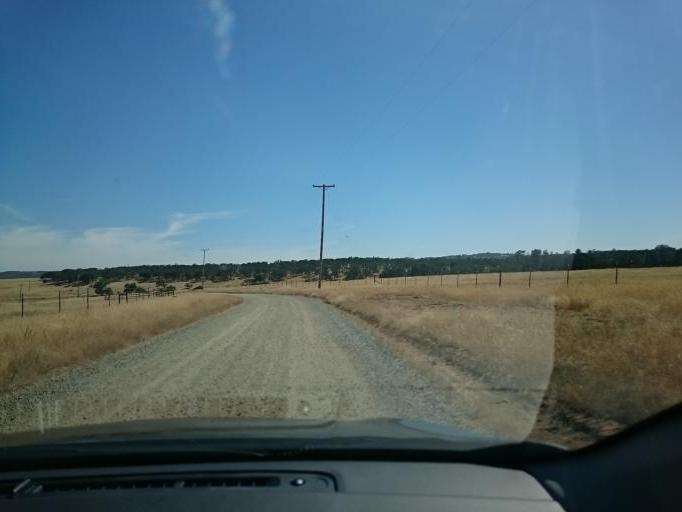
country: US
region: California
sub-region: Calaveras County
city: Copperopolis
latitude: 38.0683
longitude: -120.7399
